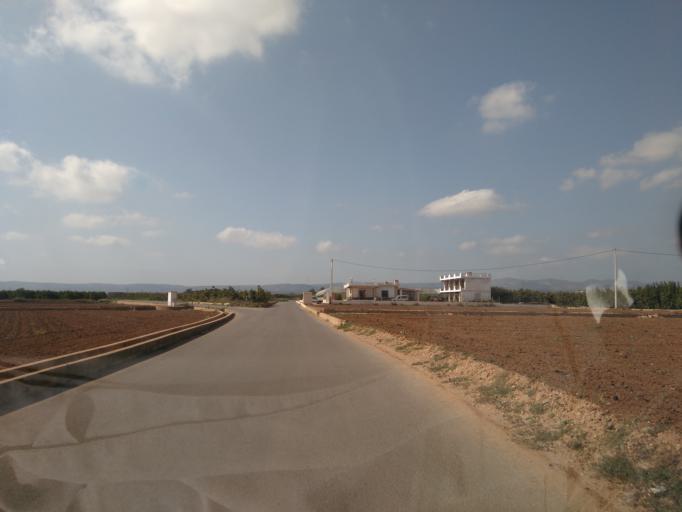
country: ES
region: Valencia
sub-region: Provincia de Valencia
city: L'Alcudia
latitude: 39.1895
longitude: -0.5246
